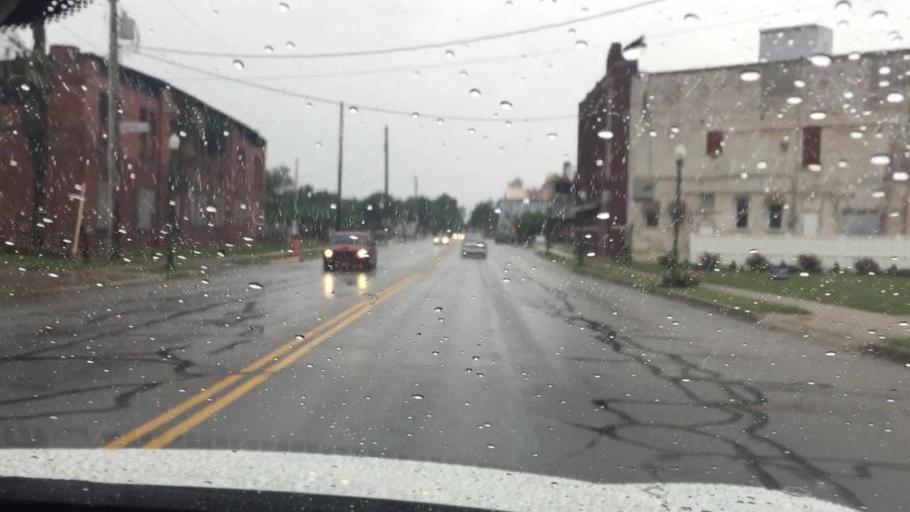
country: US
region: Ohio
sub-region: Champaign County
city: Urbana
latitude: 40.1086
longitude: -83.7585
